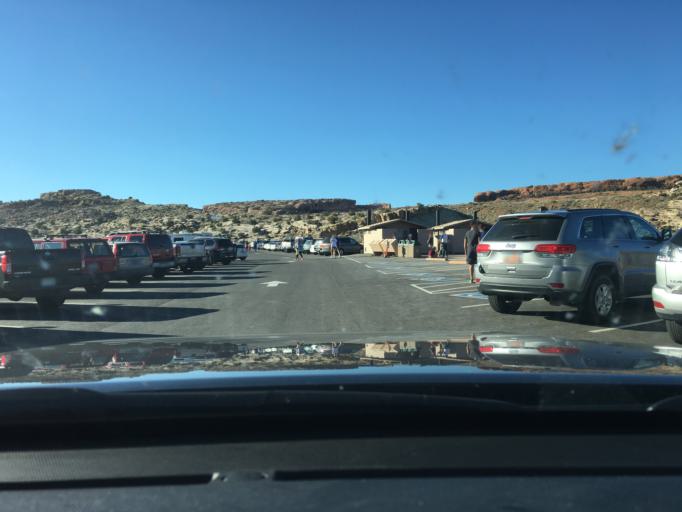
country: US
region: Utah
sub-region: Grand County
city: Moab
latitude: 38.7354
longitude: -109.5205
